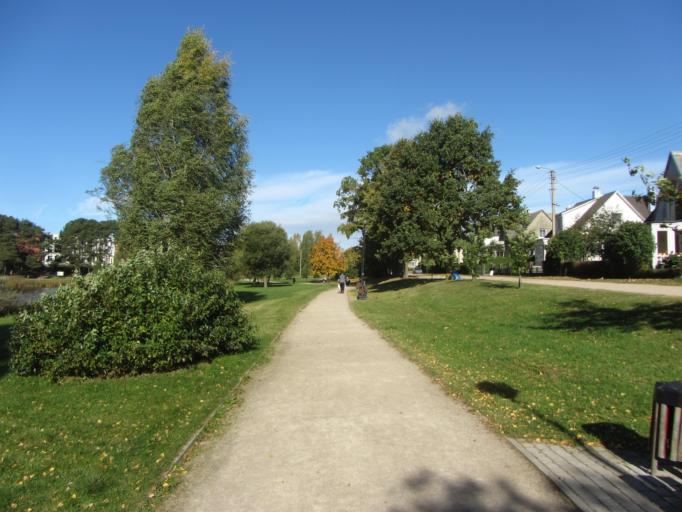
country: LT
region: Utenos apskritis
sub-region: Utena
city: Utena
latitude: 55.5066
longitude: 25.6070
